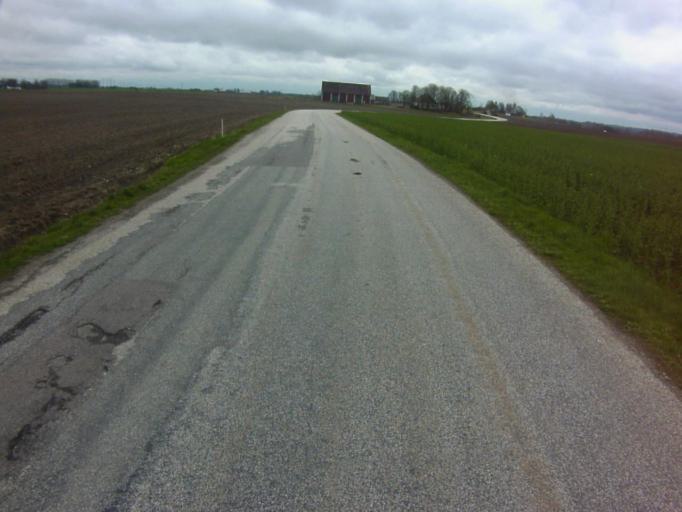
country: SE
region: Skane
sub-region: Kavlinge Kommun
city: Kaevlinge
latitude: 55.8006
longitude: 13.1594
